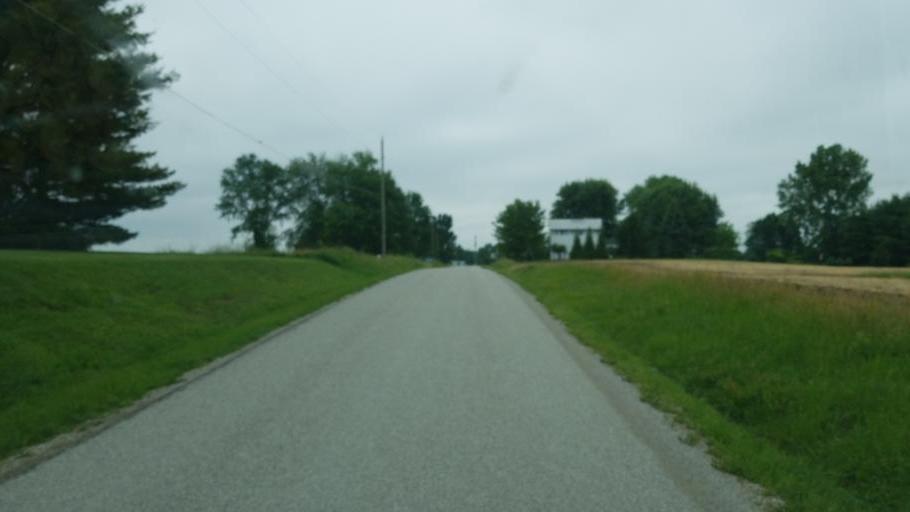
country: US
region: Ohio
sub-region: Knox County
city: Centerburg
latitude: 40.3144
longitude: -82.7412
